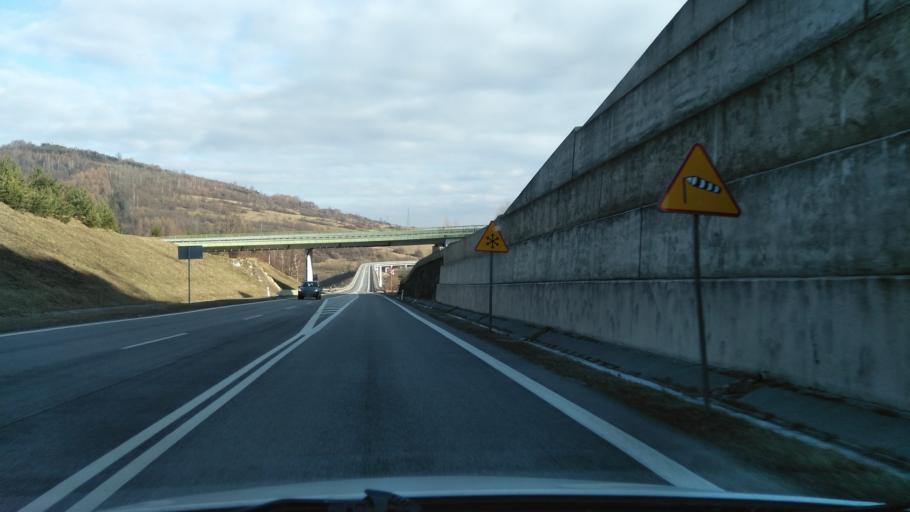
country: PL
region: Silesian Voivodeship
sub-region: Powiat zywiecki
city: Milowka
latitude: 49.5637
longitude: 19.0656
